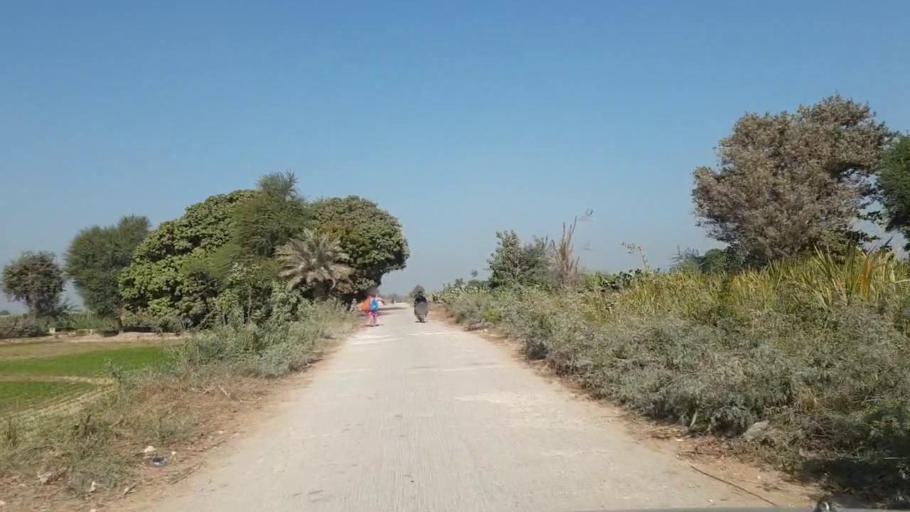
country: PK
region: Sindh
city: Matiari
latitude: 25.5770
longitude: 68.6050
